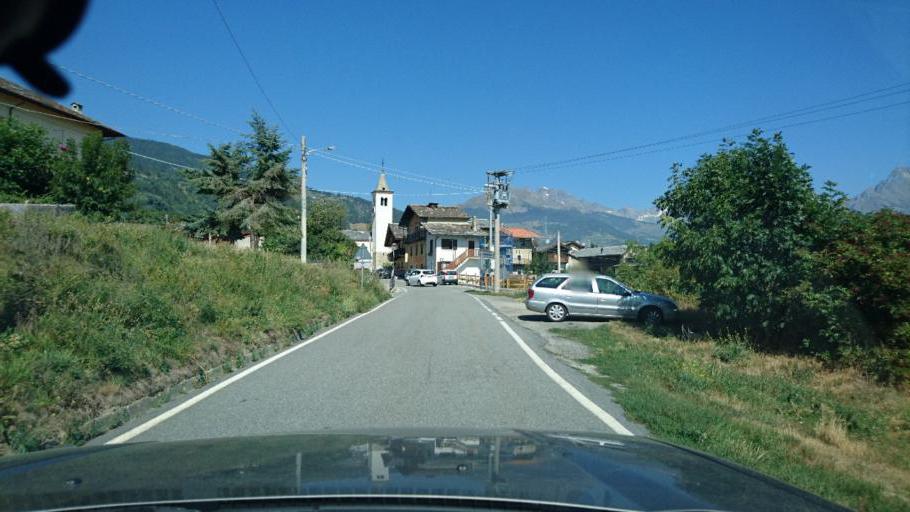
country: IT
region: Aosta Valley
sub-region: Valle d'Aosta
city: Gignod
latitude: 45.7603
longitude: 7.3012
